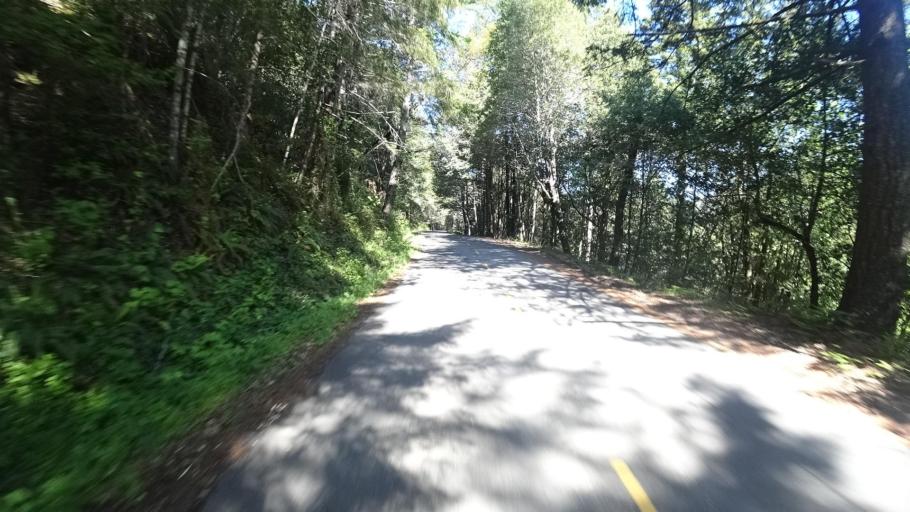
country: US
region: California
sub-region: Humboldt County
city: Rio Dell
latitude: 40.2686
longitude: -124.2027
